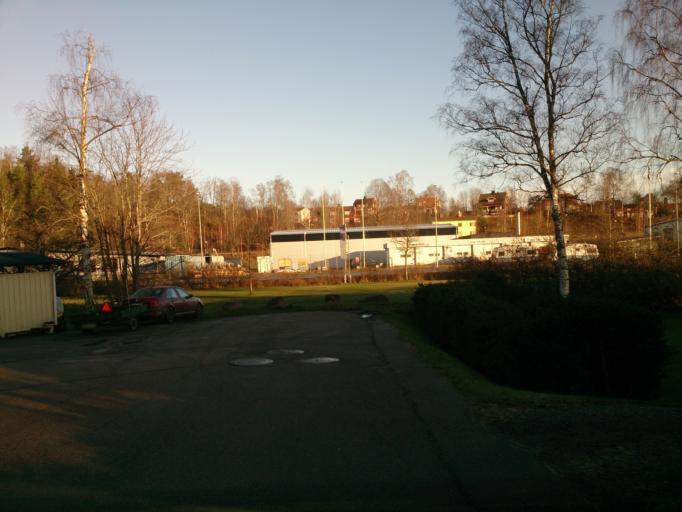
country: SE
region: OEstergoetland
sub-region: Atvidabergs Kommun
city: Atvidaberg
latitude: 58.2034
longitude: 15.9977
